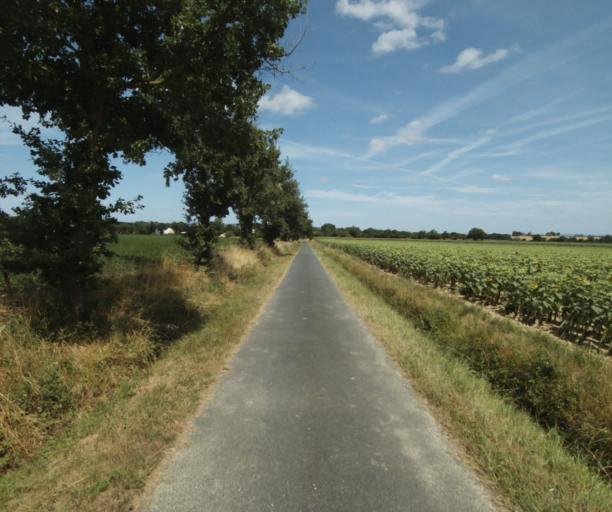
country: FR
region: Midi-Pyrenees
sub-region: Departement du Tarn
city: Soreze
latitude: 43.4985
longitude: 2.0654
